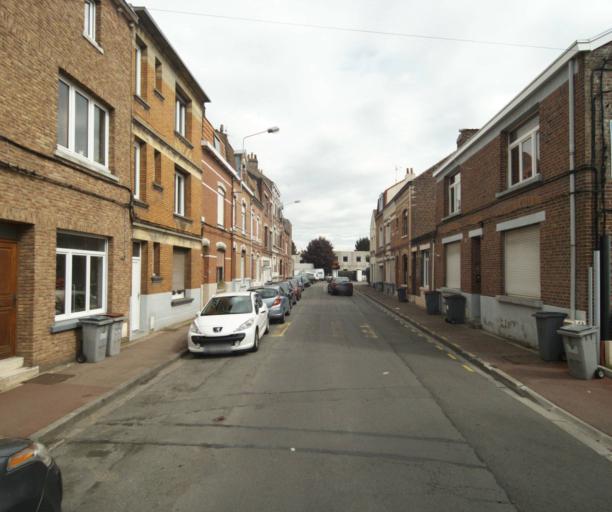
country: FR
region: Nord-Pas-de-Calais
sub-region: Departement du Nord
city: Marcq-en-Baroeul
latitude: 50.6589
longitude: 3.0818
